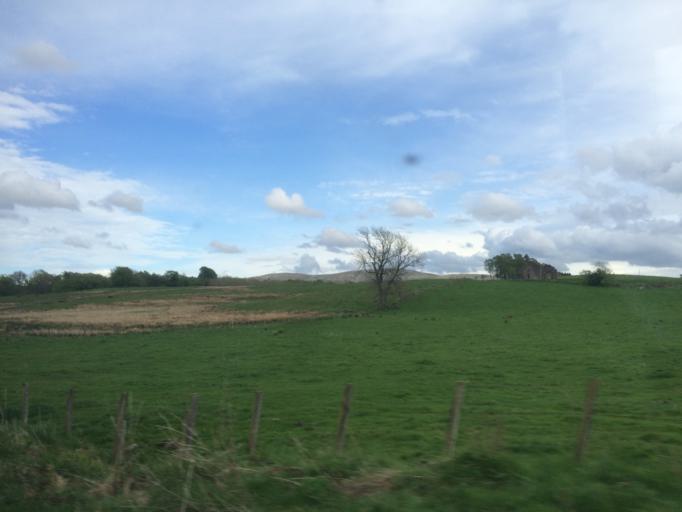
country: GB
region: Scotland
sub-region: Stirling
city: Dunblane
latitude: 56.2315
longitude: -3.9201
